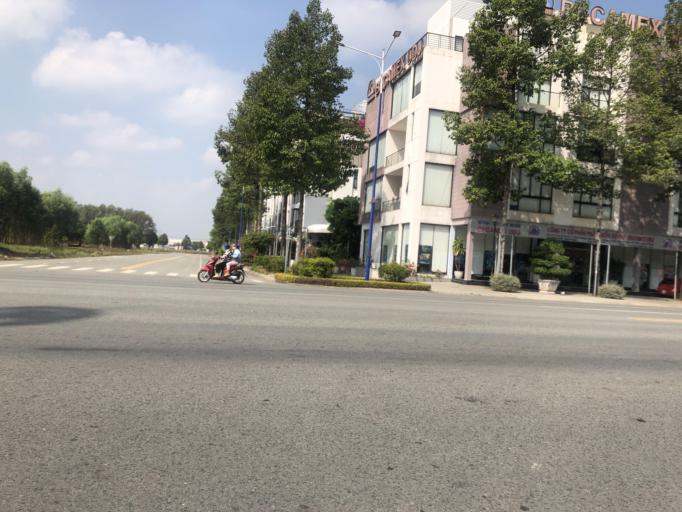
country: VN
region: Binh Duong
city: Thu Dau Mot
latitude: 11.0687
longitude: 106.6768
